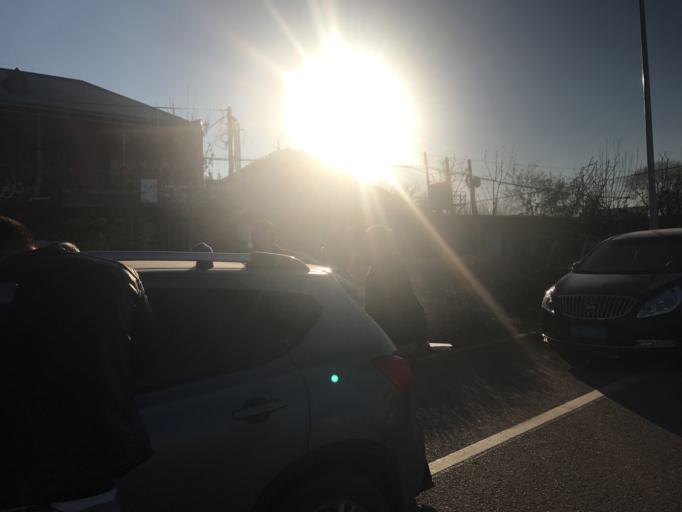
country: CN
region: Xinjiang Uygur Zizhiqu
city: Yili
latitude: 43.9300
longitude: 81.3809
